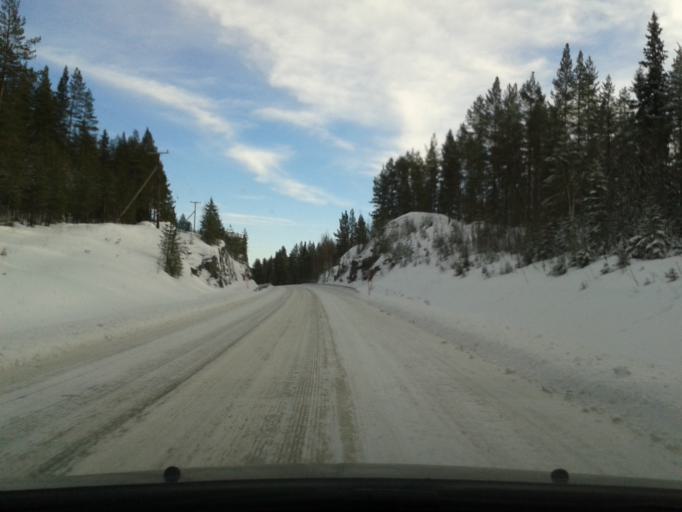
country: SE
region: Vaesterbotten
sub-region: Asele Kommun
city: Asele
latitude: 64.3568
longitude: 16.9724
